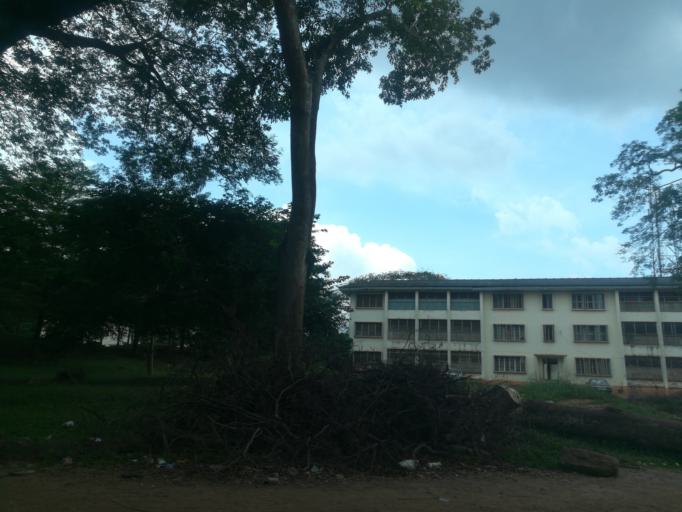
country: NG
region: Oyo
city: Ibadan
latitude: 7.4421
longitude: 3.9056
